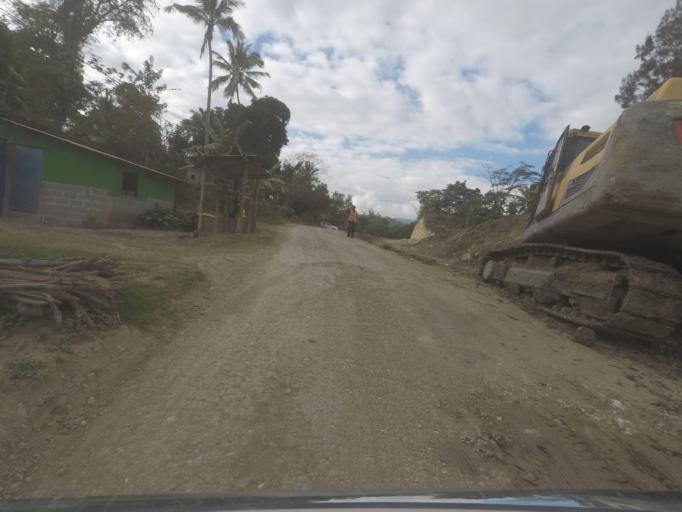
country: TL
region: Baucau
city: Venilale
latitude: -8.6257
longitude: 126.3828
